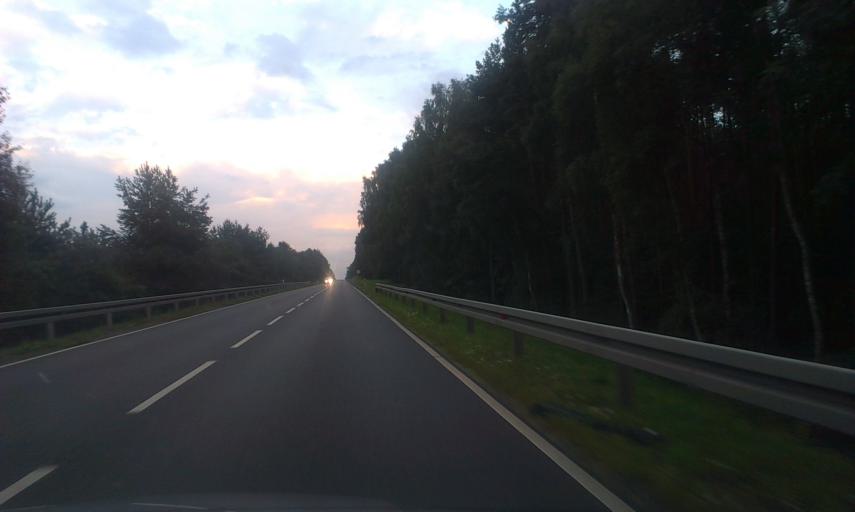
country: PL
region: West Pomeranian Voivodeship
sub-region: Powiat koszalinski
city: Sianow
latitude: 54.1190
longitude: 16.3139
